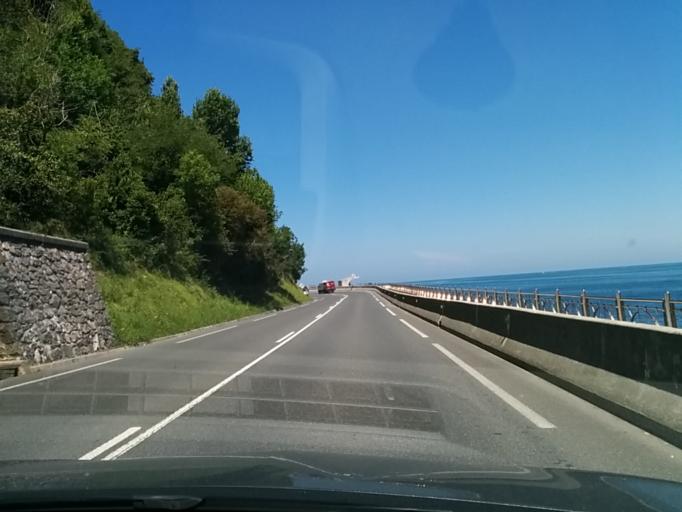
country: ES
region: Basque Country
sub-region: Provincia de Guipuzcoa
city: Getaria
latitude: 43.2937
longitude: -2.1913
